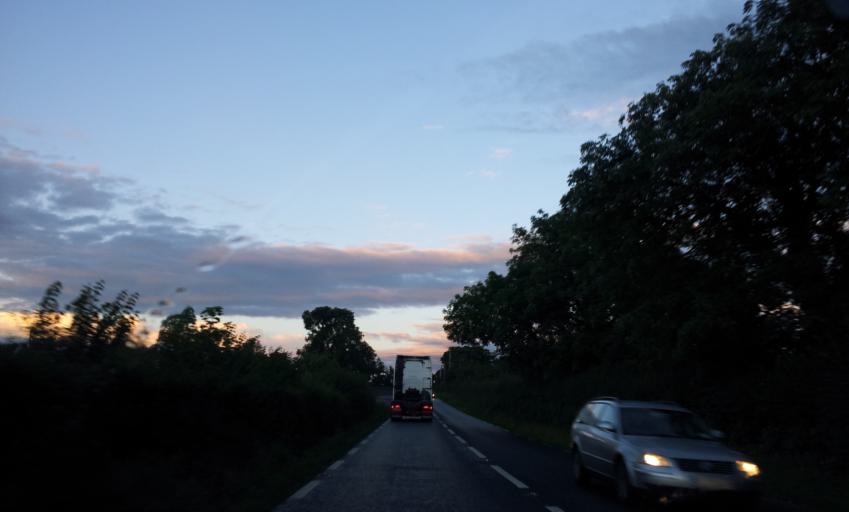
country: IE
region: Munster
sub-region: County Limerick
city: Adare
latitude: 52.5742
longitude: -8.7712
